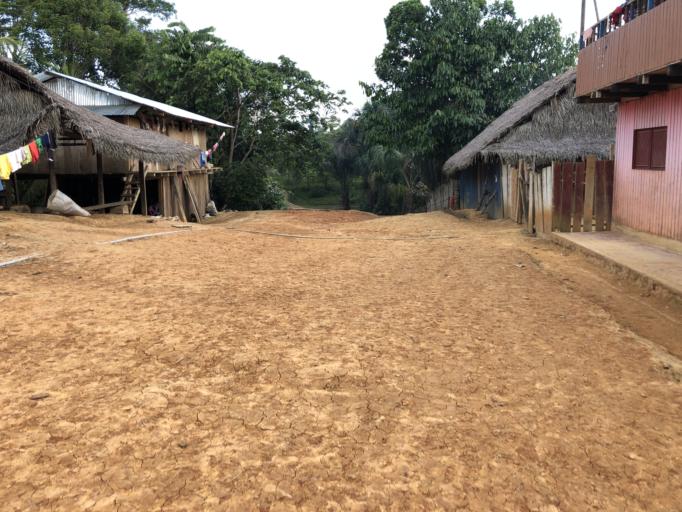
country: PE
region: Loreto
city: Puerto Galilea
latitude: -4.0543
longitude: -77.7616
